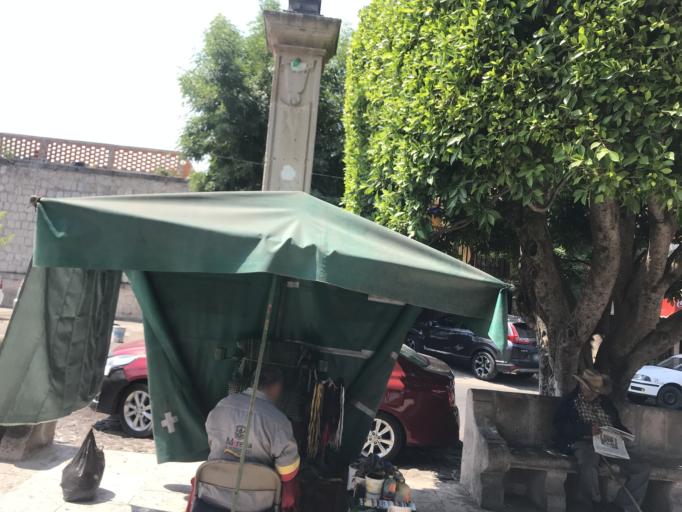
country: MX
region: Michoacan
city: Morelia
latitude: 19.6741
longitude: -101.1906
